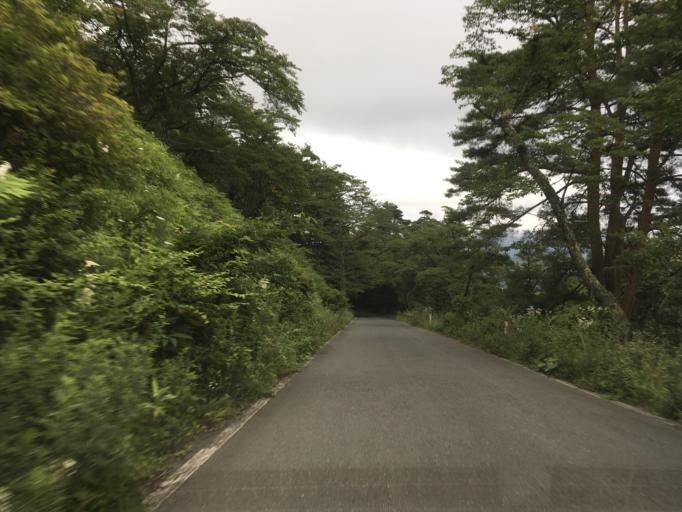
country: JP
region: Iwate
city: Ofunato
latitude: 38.9583
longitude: 141.4497
